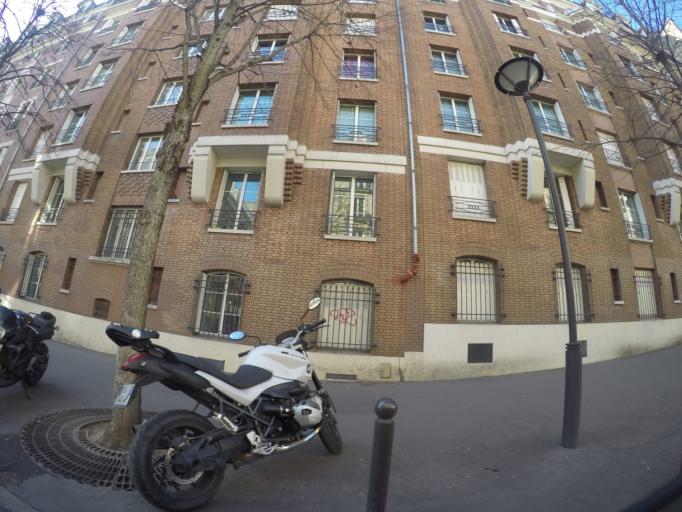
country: FR
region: Ile-de-France
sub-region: Paris
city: Paris
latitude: 48.8764
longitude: 2.3512
